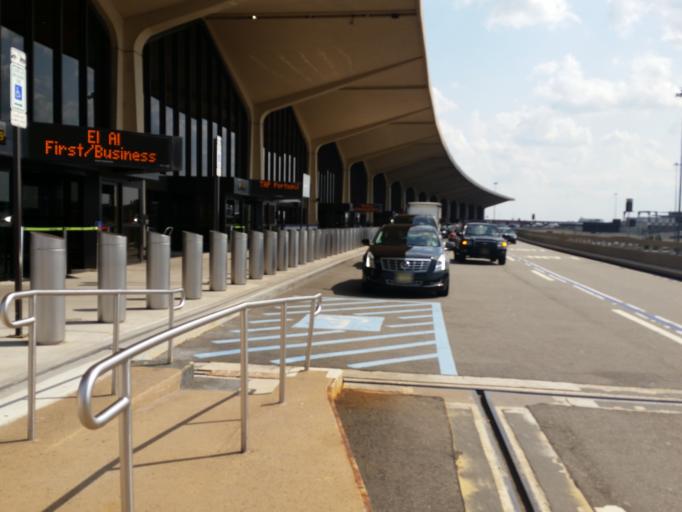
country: US
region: New Jersey
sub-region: Union County
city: Elizabeth
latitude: 40.6916
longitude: -74.1769
